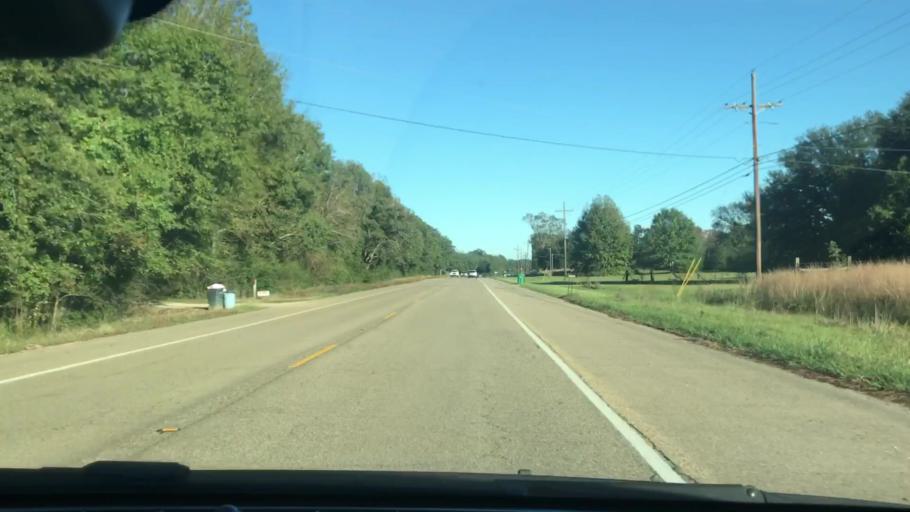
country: US
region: Louisiana
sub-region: Washington Parish
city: Bogalusa
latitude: 30.6092
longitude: -89.8932
